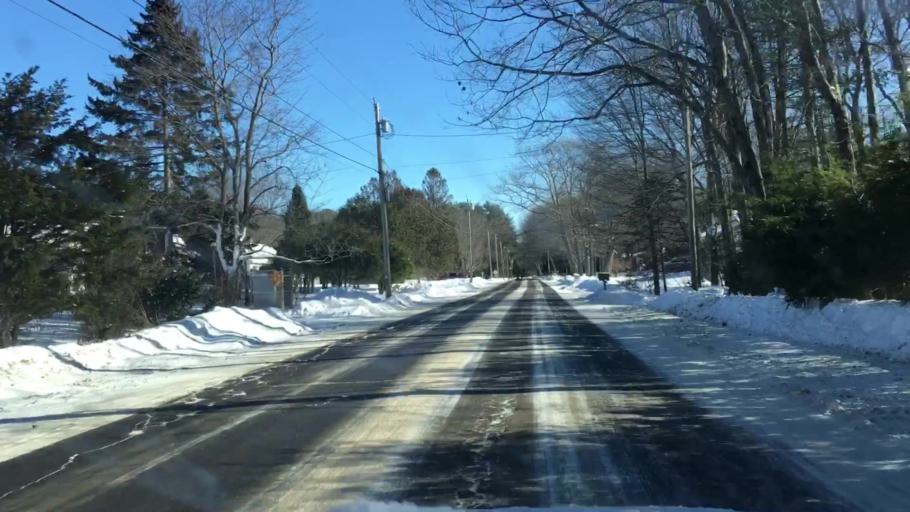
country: US
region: Maine
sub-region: Cumberland County
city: Brunswick
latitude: 43.8935
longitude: -69.9796
